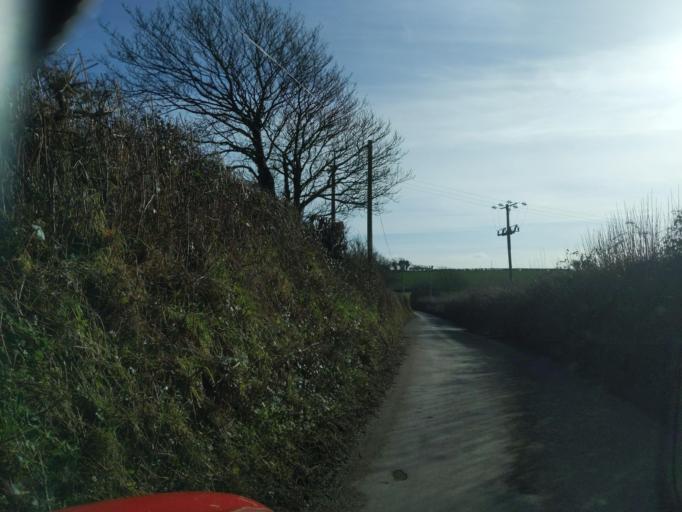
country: GB
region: England
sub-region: Devon
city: Kingsbridge
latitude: 50.3330
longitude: -3.7198
